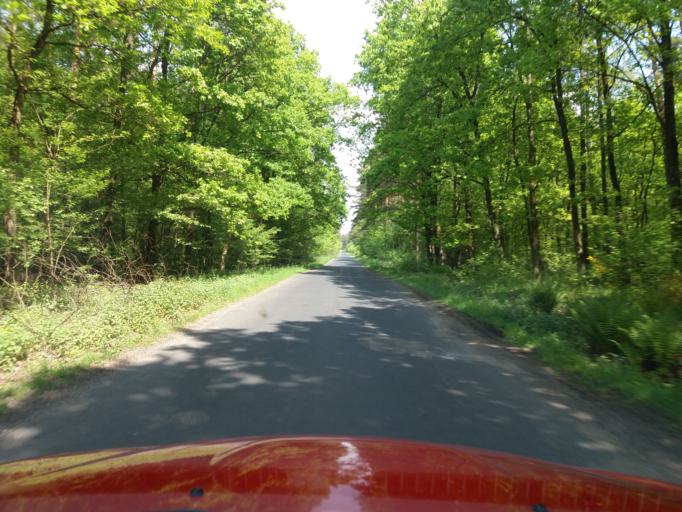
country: PL
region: West Pomeranian Voivodeship
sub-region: Powiat choszczenski
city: Bierzwnik
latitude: 53.1234
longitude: 15.6544
